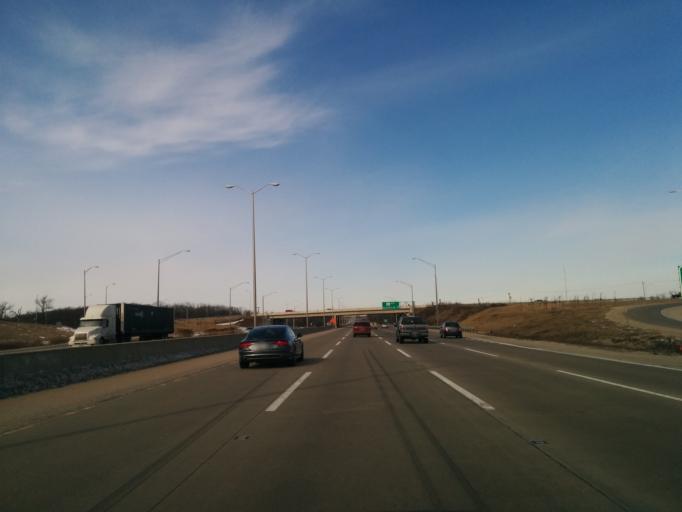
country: US
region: Illinois
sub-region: Lake County
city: Gurnee
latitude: 42.3434
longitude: -87.9214
